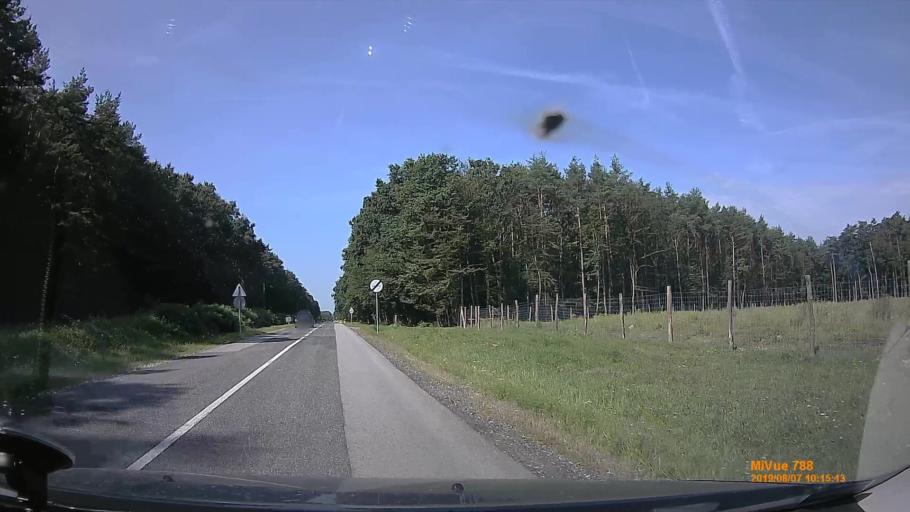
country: HU
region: Zala
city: Lenti
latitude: 46.6469
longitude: 16.6189
